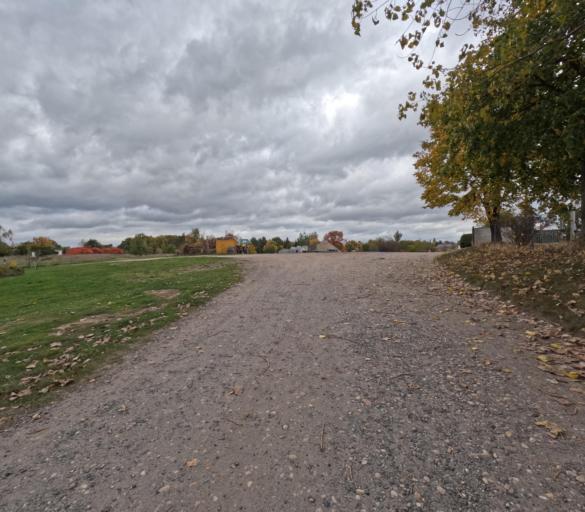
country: DE
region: Saxony
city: Grimma
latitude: 51.2454
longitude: 12.7232
